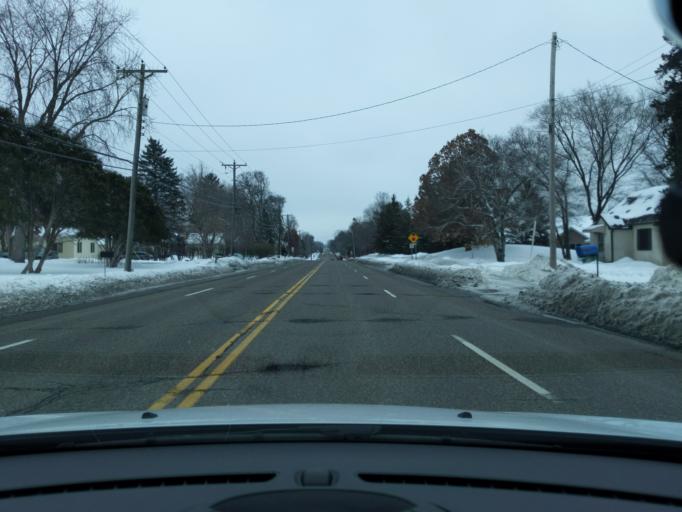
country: US
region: Minnesota
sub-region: Ramsey County
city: Roseville
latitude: 45.0207
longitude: -93.1295
